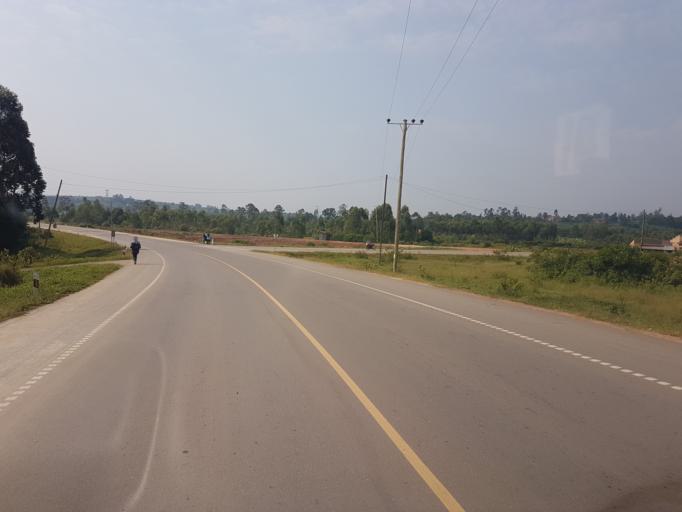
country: UG
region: Western Region
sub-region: Mbarara District
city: Bwizibwera
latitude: -0.6365
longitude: 30.6035
